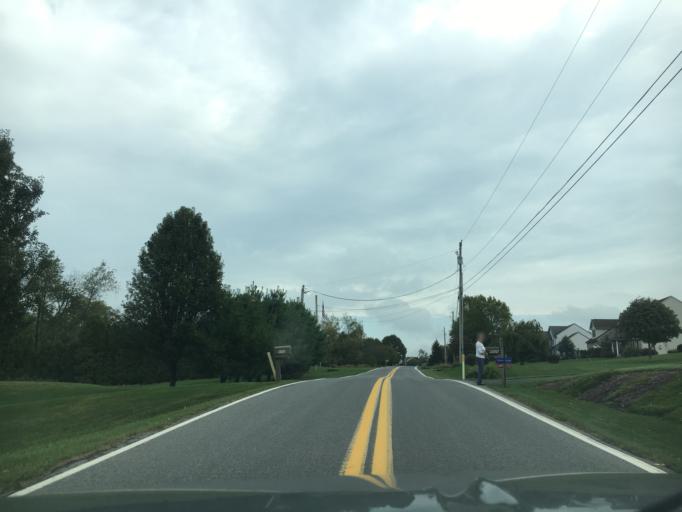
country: US
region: Pennsylvania
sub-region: Berks County
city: Fleetwood
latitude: 40.4541
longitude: -75.7558
